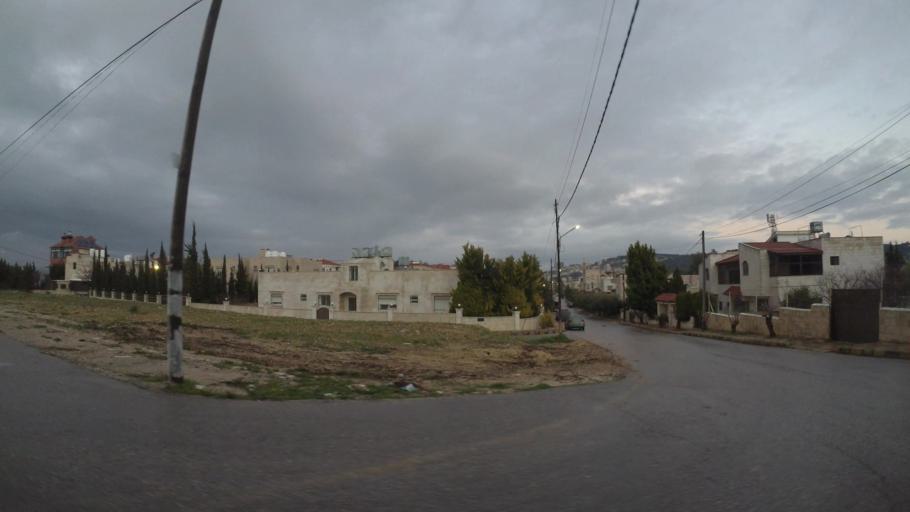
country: JO
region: Amman
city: Al Jubayhah
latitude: 32.0296
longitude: 35.8107
